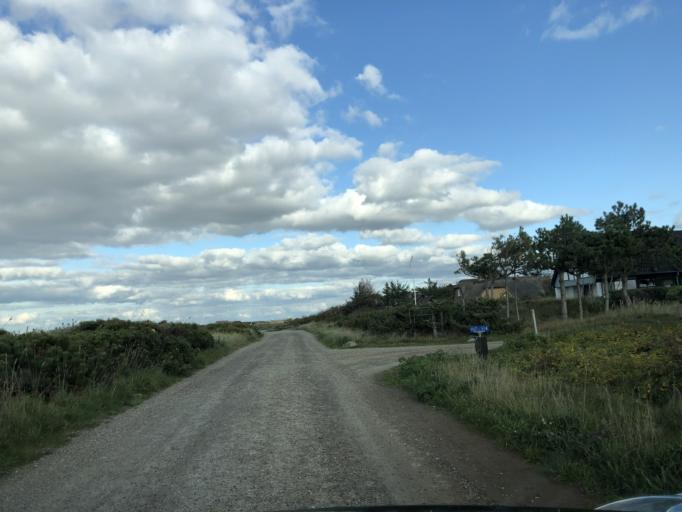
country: DK
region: Central Jutland
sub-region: Holstebro Kommune
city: Ulfborg
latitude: 56.3274
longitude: 8.1438
